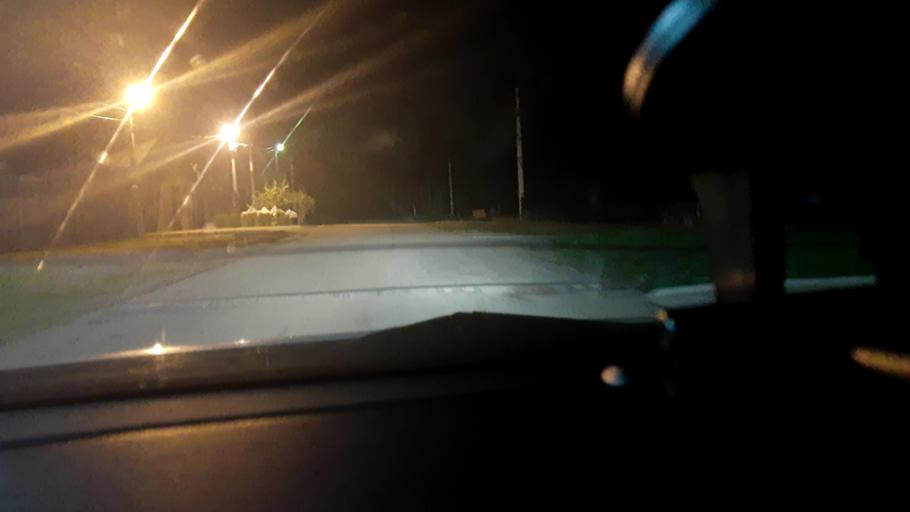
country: RU
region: Bashkortostan
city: Ufa
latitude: 54.6647
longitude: 56.0567
